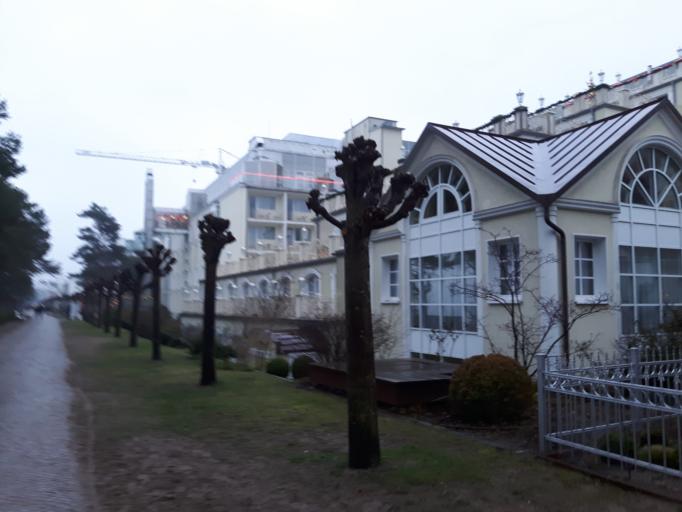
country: DE
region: Mecklenburg-Vorpommern
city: Ostseebad Binz
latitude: 54.4089
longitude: 13.6035
